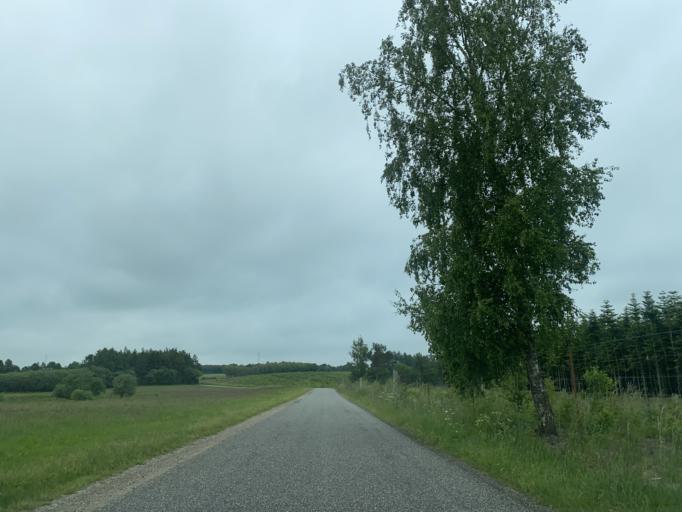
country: DK
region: Central Jutland
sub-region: Viborg Kommune
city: Bjerringbro
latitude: 56.3548
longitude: 9.6264
